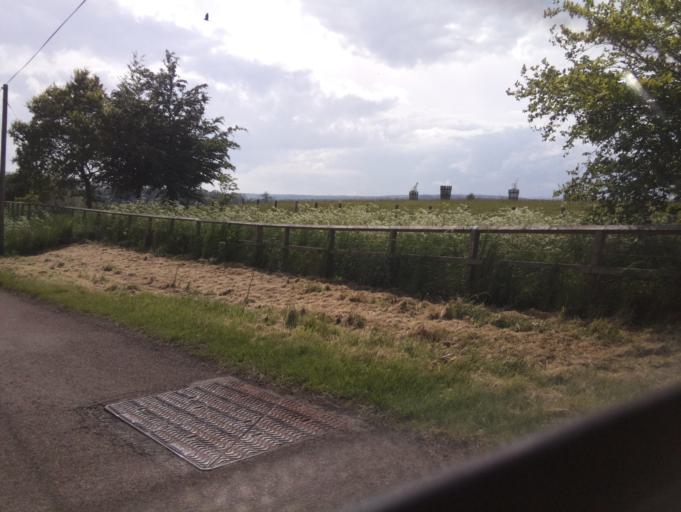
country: GB
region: England
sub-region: Northumberland
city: Alnwick
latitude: 55.4247
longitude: -1.7025
